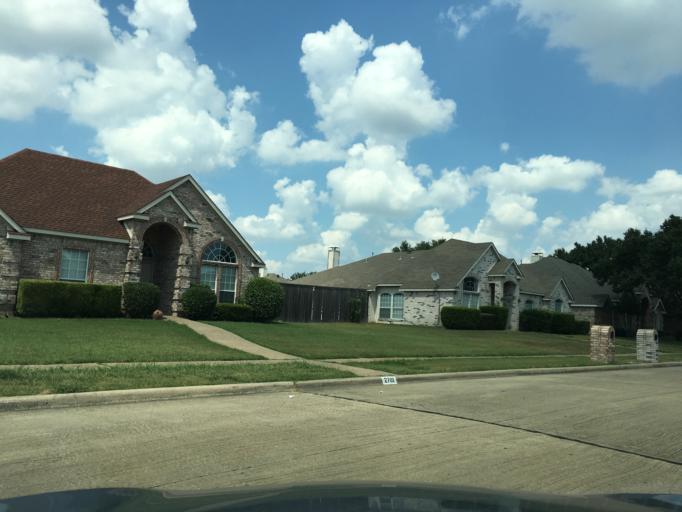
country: US
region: Texas
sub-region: Dallas County
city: Garland
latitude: 32.9419
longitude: -96.6443
